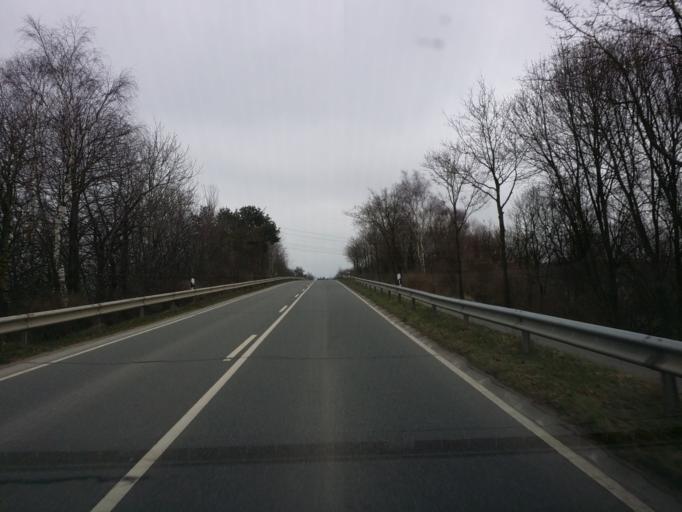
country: DE
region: Schleswig-Holstein
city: Schulldorf
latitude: 54.3133
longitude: 9.7446
